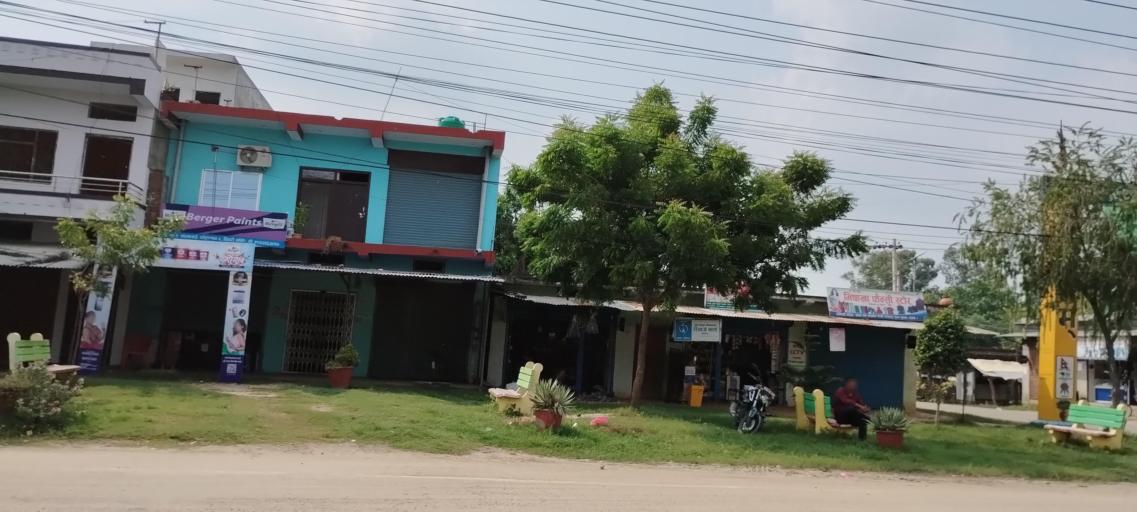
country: NP
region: Mid Western
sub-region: Bheri Zone
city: Nepalgunj
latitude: 28.1622
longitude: 81.6723
